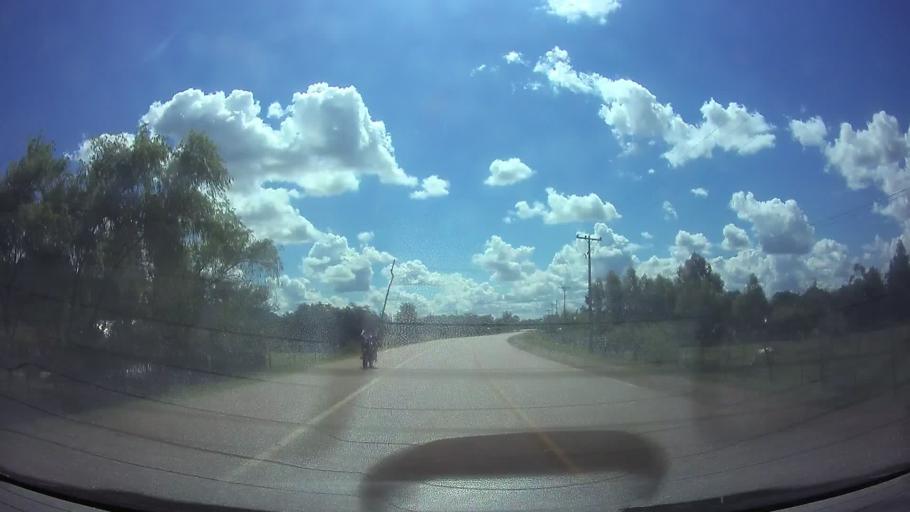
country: PY
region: Guaira
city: Itape
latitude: -25.9163
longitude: -56.6923
